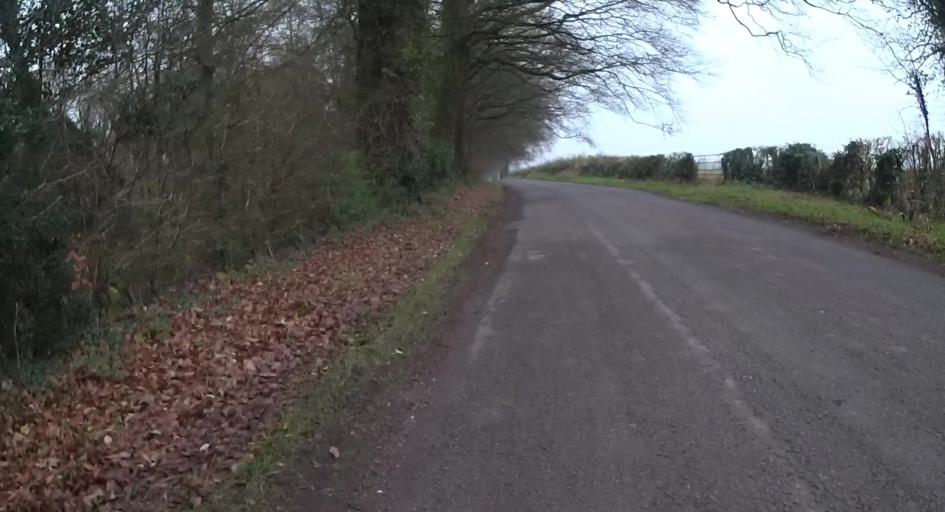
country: GB
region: England
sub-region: Hampshire
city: Kings Worthy
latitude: 51.1256
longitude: -1.2116
